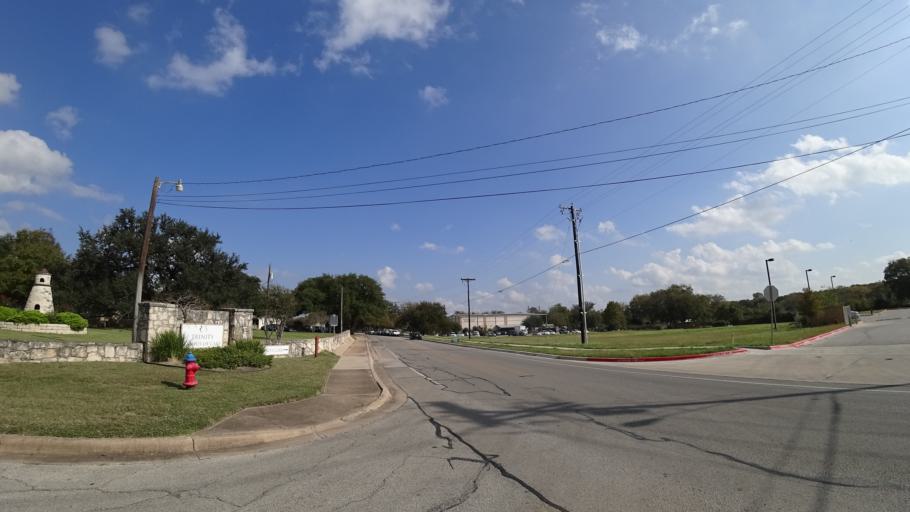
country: US
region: Texas
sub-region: Williamson County
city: Round Rock
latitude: 30.5112
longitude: -97.6694
